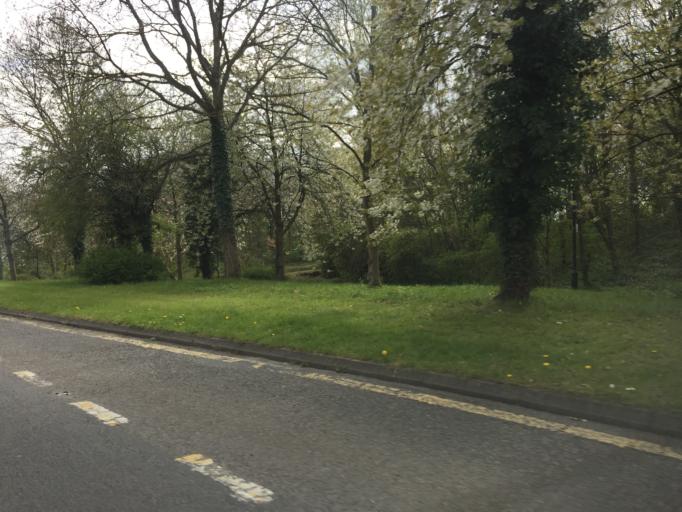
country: GB
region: England
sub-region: Milton Keynes
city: Milton Keynes
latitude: 52.0657
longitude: -0.7605
